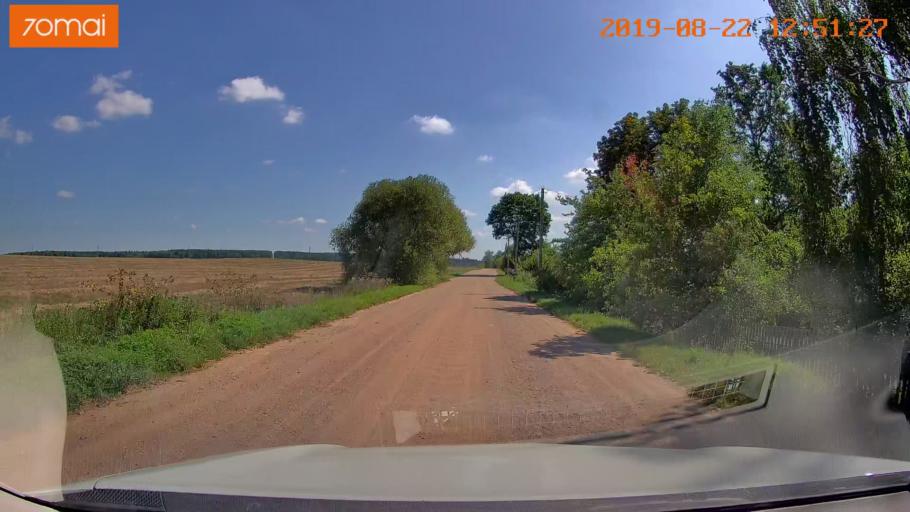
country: BY
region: Minsk
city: Prawdzinski
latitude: 53.4579
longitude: 27.6553
